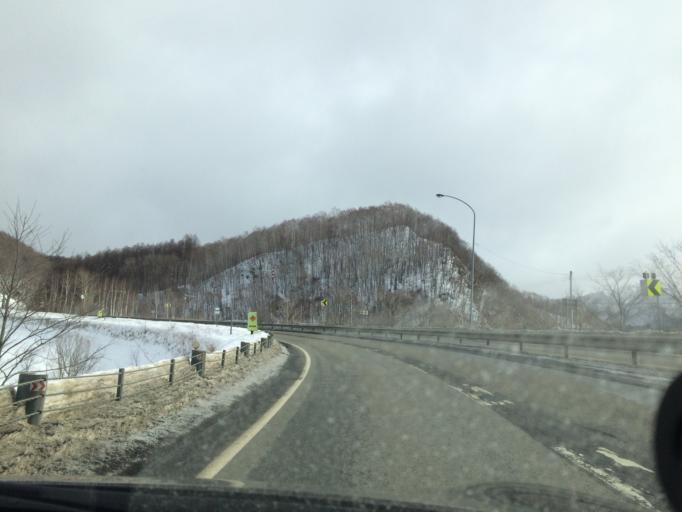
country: JP
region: Hokkaido
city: Shimo-furano
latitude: 42.8858
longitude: 142.2556
